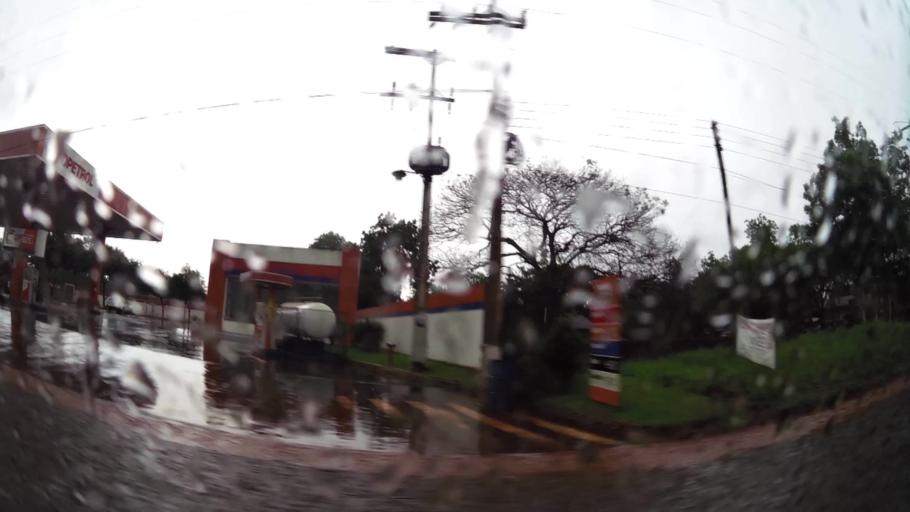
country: PY
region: Alto Parana
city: Presidente Franco
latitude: -25.5209
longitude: -54.6758
